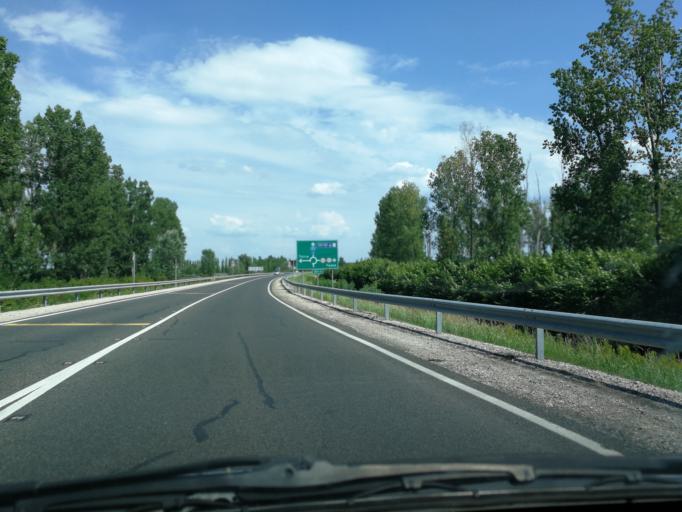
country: HU
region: Tolna
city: Szekszard
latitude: 46.3891
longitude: 18.7145
